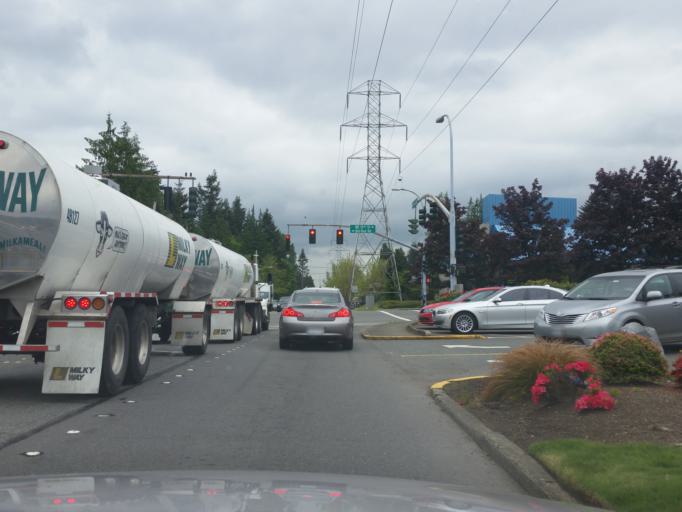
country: US
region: Washington
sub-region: King County
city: Bellevue
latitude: 47.6204
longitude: -122.1751
